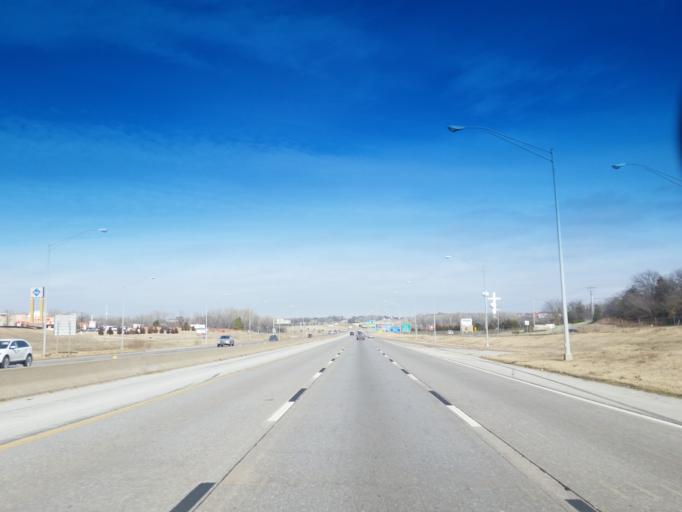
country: US
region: Oklahoma
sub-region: Oklahoma County
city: Edmond
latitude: 35.6400
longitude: -97.4247
